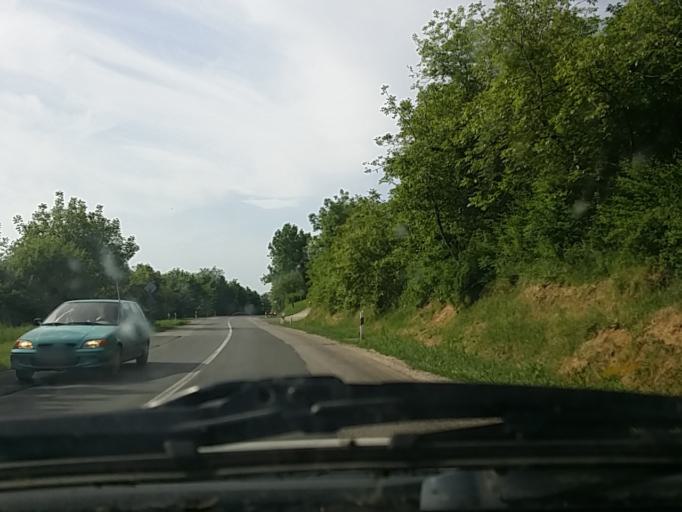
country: HU
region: Baranya
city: Harkany
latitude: 45.8966
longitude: 18.2335
